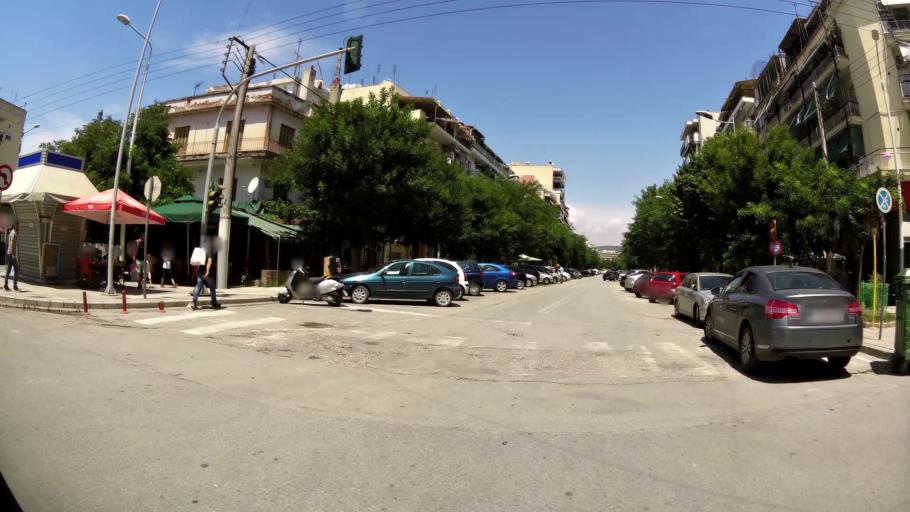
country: GR
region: Central Macedonia
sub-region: Nomos Thessalonikis
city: Triandria
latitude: 40.6072
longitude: 22.9601
